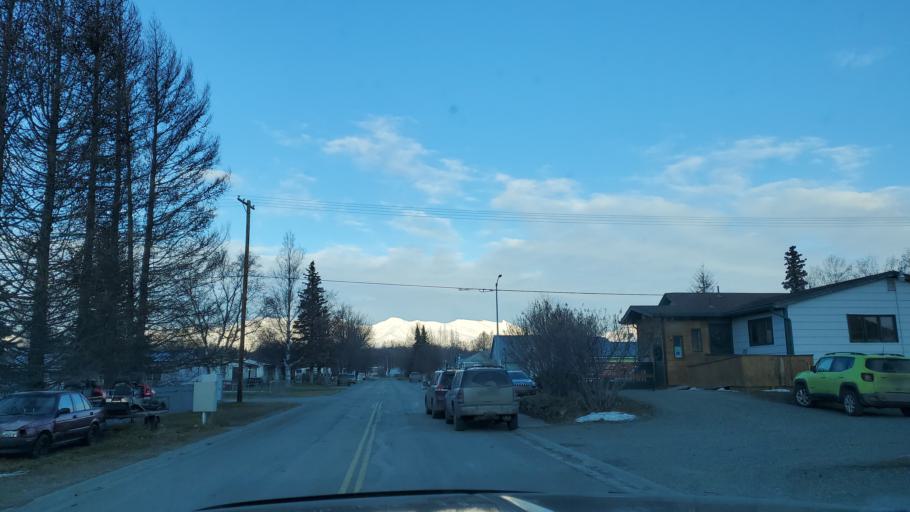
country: US
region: Alaska
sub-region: Matanuska-Susitna Borough
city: Palmer
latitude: 61.6029
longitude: -149.1165
